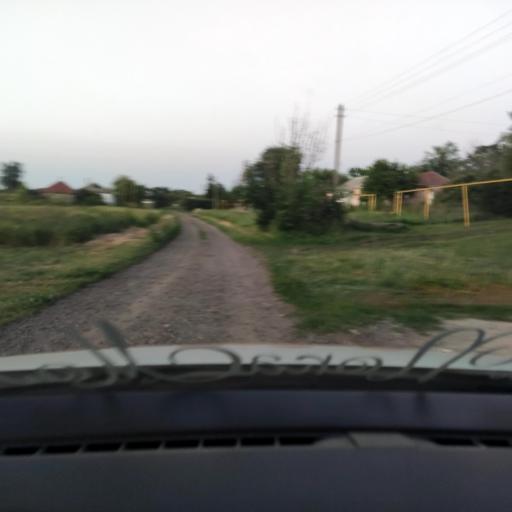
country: RU
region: Voronezj
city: Novovoronezh
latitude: 51.4215
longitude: 39.3348
